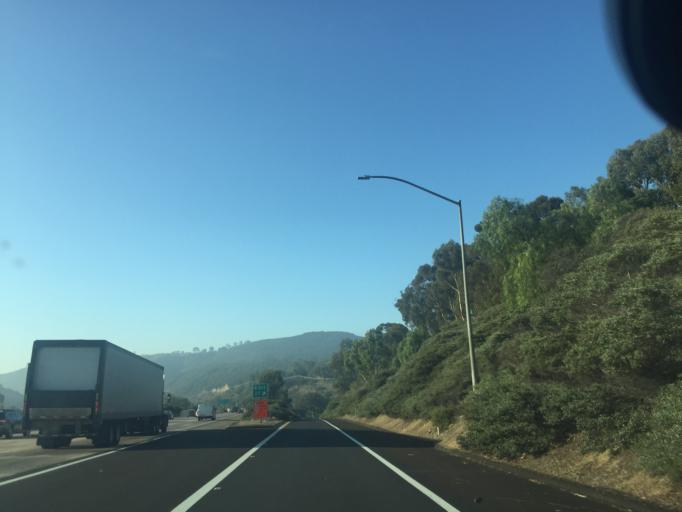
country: US
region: California
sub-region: San Diego County
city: La Jolla
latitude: 32.8536
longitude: -117.2327
